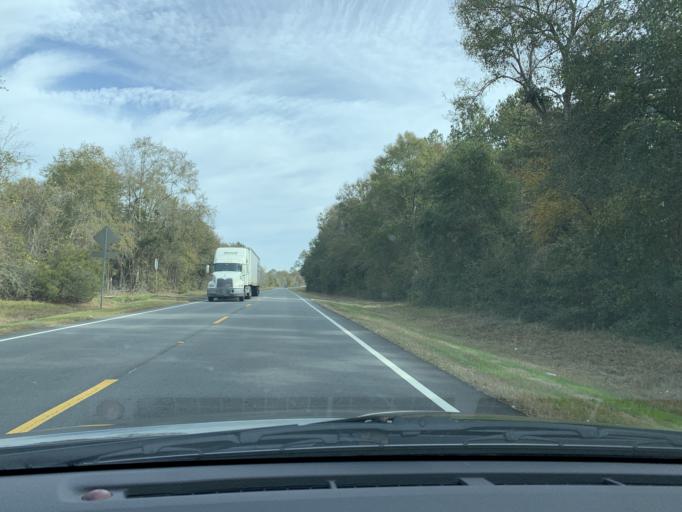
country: US
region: Georgia
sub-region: Wilcox County
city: Rochelle
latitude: 31.9598
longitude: -83.5973
